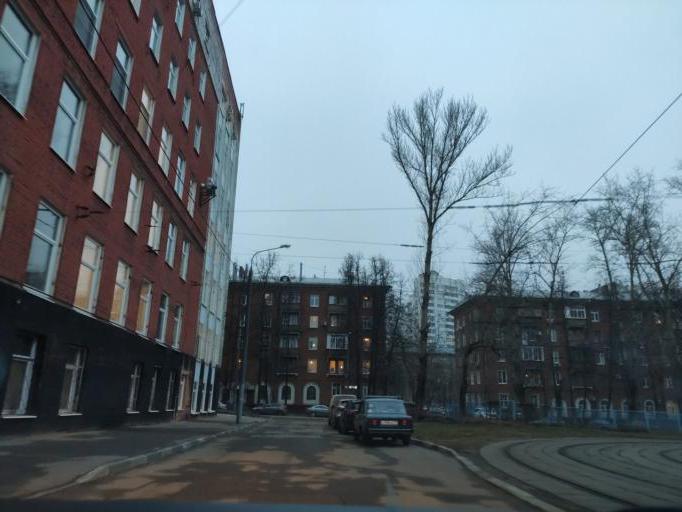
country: RU
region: Moscow
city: Novyye Cheremushki
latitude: 55.6790
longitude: 37.5837
